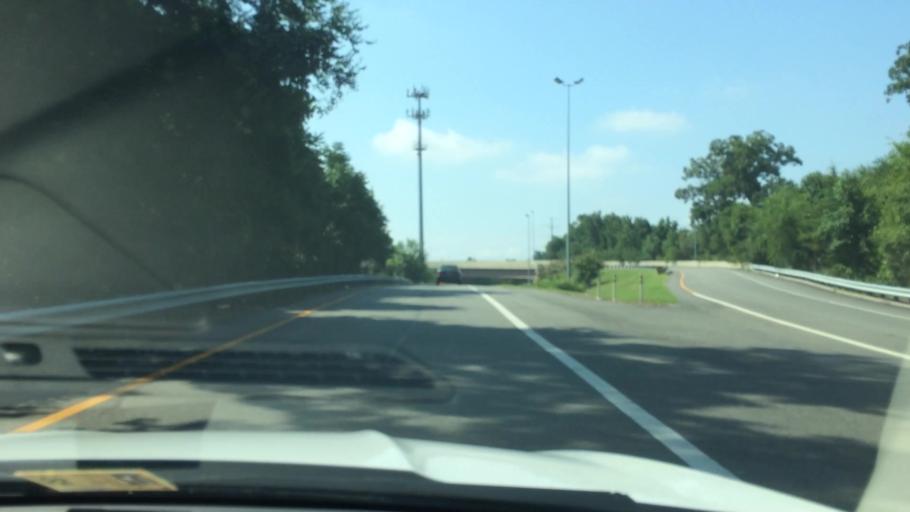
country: US
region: Virginia
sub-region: City of Hampton
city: Hampton
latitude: 37.0420
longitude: -76.3978
